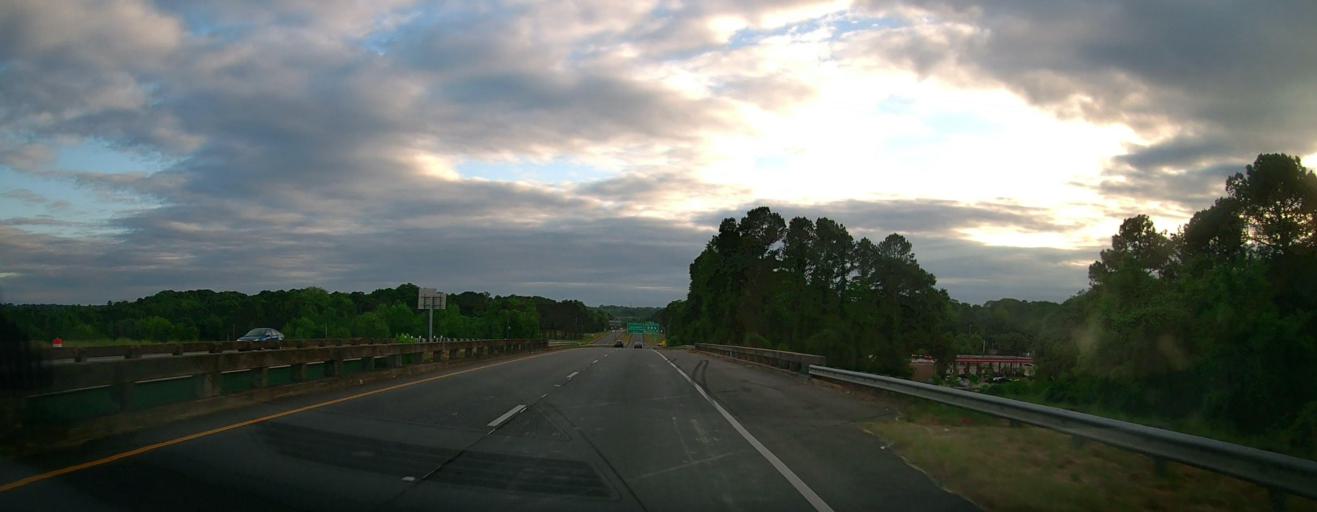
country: US
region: Georgia
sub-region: Clarke County
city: Athens
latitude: 33.9485
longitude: -83.3539
